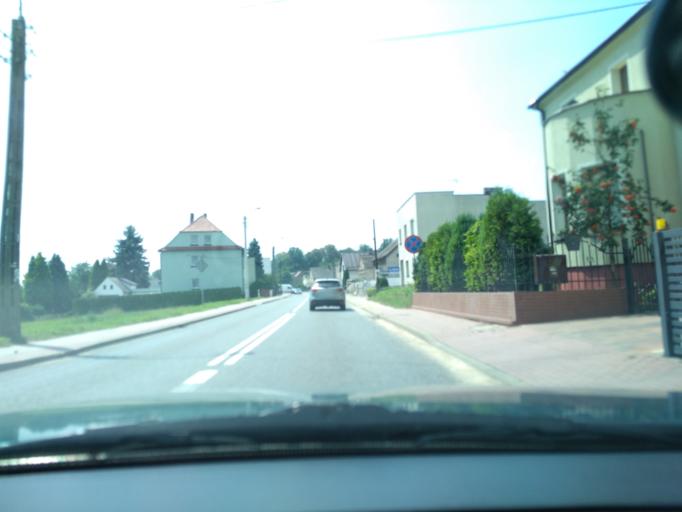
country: PL
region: Silesian Voivodeship
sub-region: Powiat raciborski
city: Raciborz
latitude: 50.0969
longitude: 18.2037
